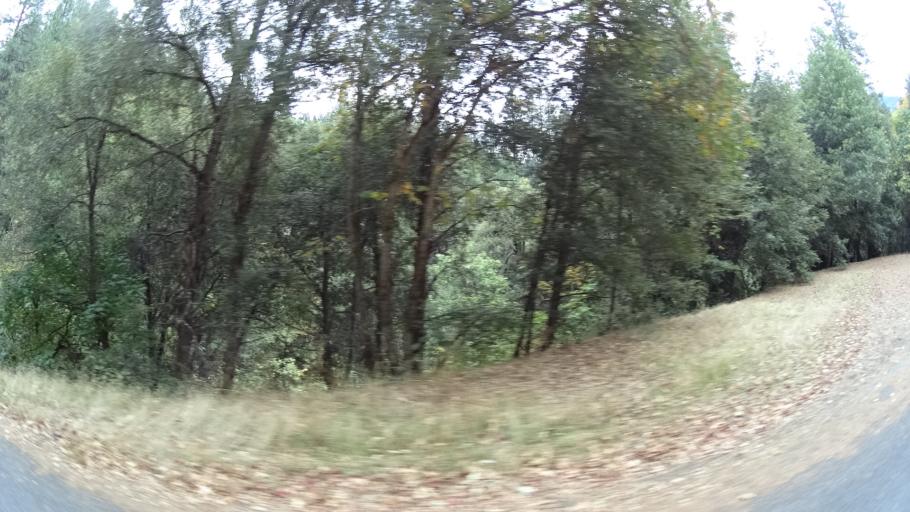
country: US
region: California
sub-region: Siskiyou County
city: Happy Camp
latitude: 41.7793
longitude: -123.3811
